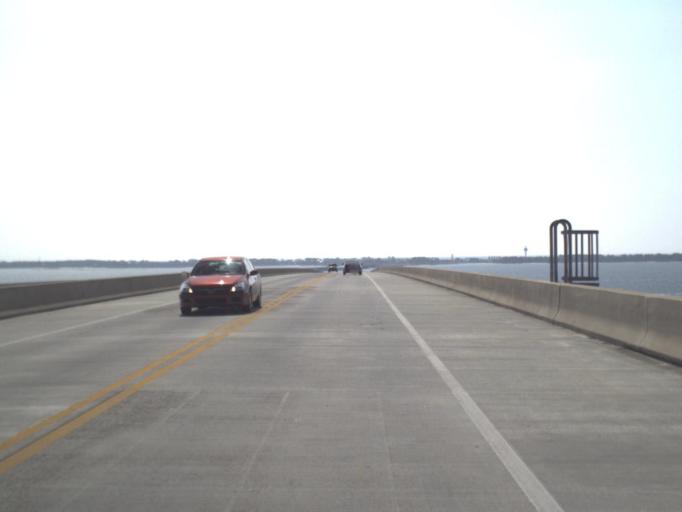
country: US
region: Florida
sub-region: Franklin County
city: Eastpoint
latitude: 29.6836
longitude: -84.8803
